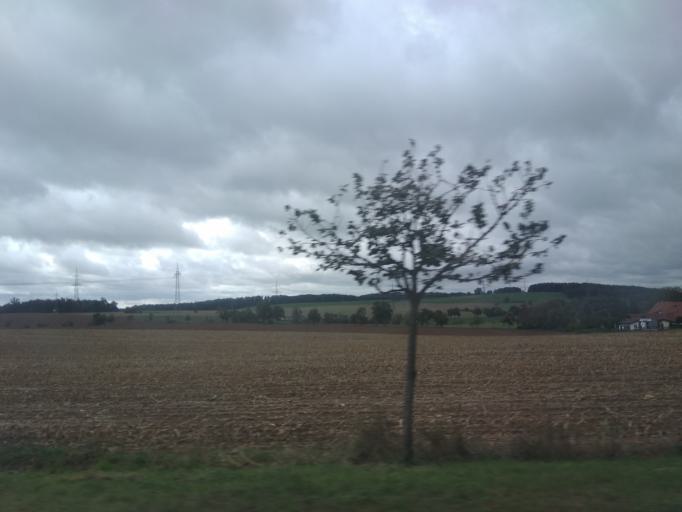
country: DE
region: Baden-Wuerttemberg
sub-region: Karlsruhe Region
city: Mosbach
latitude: 49.3458
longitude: 9.1829
